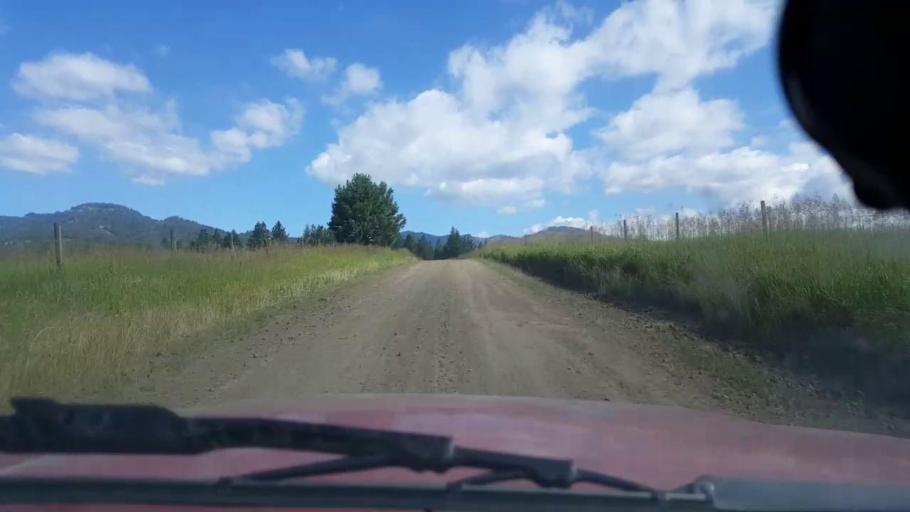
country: US
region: Washington
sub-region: Asotin County
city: Asotin
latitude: 46.0344
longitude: -117.4075
